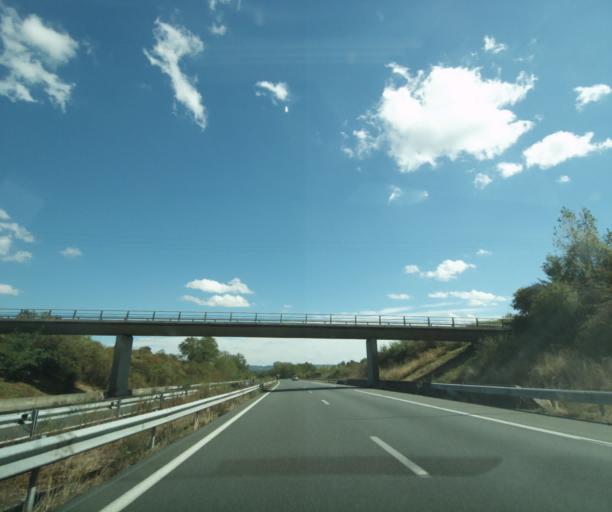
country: FR
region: Aquitaine
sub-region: Departement du Lot-et-Garonne
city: Fourques-sur-Garonne
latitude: 44.3795
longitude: 0.2144
